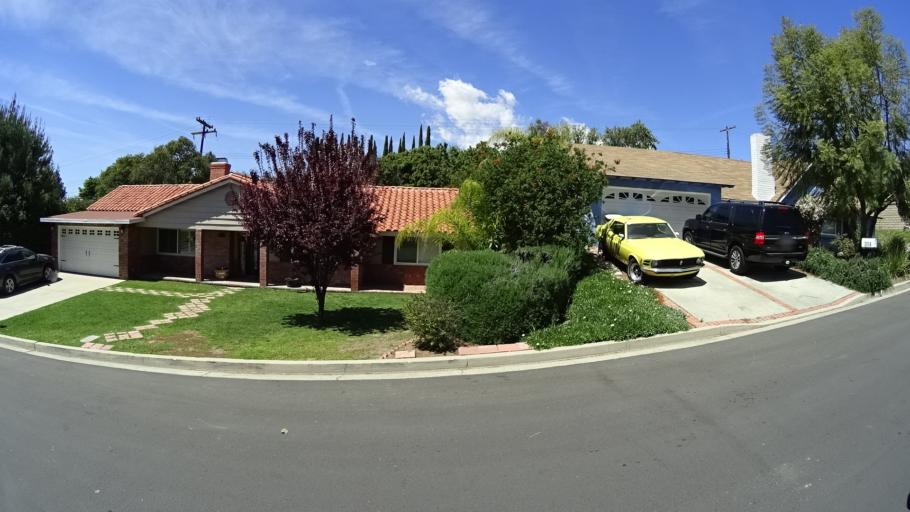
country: US
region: California
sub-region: Ventura County
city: Thousand Oaks
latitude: 34.2170
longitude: -118.8562
